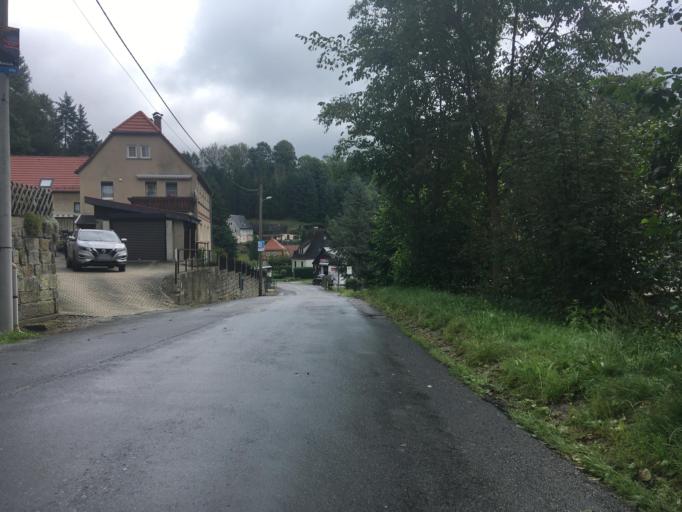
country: DE
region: Saxony
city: Bad Schandau
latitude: 50.8889
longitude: 14.2058
